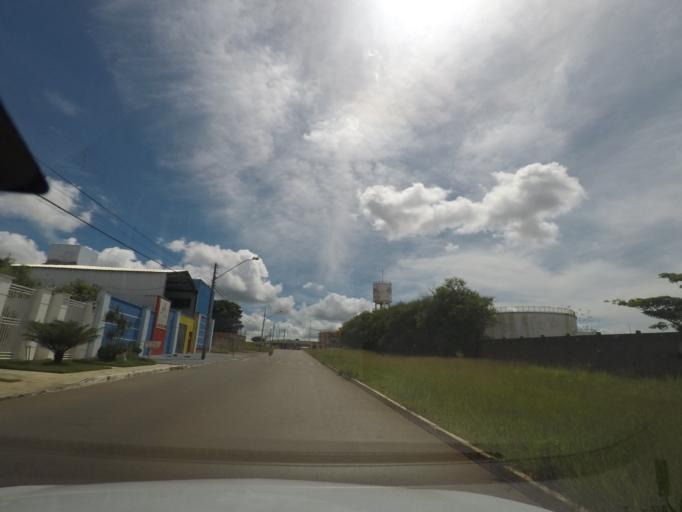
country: BR
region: Goias
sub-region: Goiania
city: Goiania
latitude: -16.7550
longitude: -49.3468
